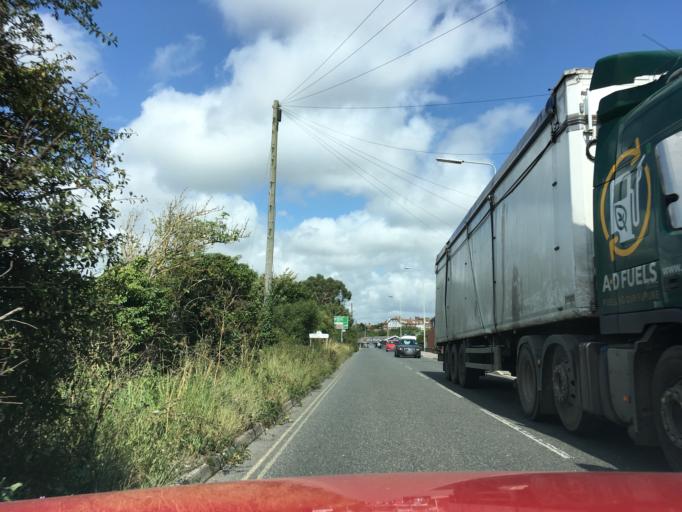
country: GB
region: England
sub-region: East Sussex
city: Rye
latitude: 50.9454
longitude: 0.7298
